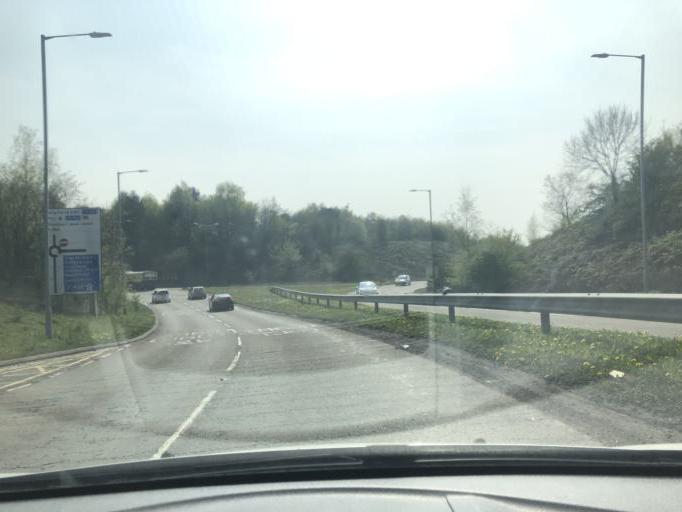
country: GB
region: England
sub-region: Borough of Stockport
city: Bredbury
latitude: 53.4258
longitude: -2.1228
